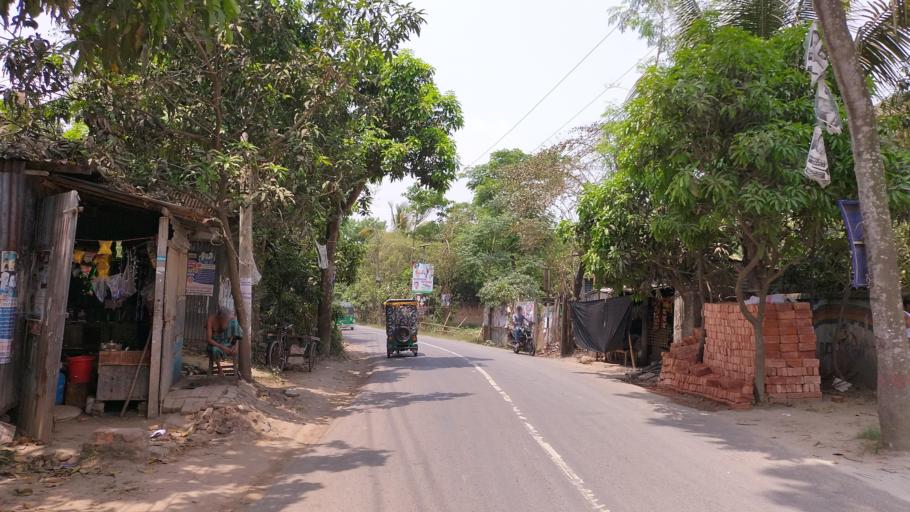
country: BD
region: Dhaka
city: Azimpur
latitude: 23.7286
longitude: 90.2931
